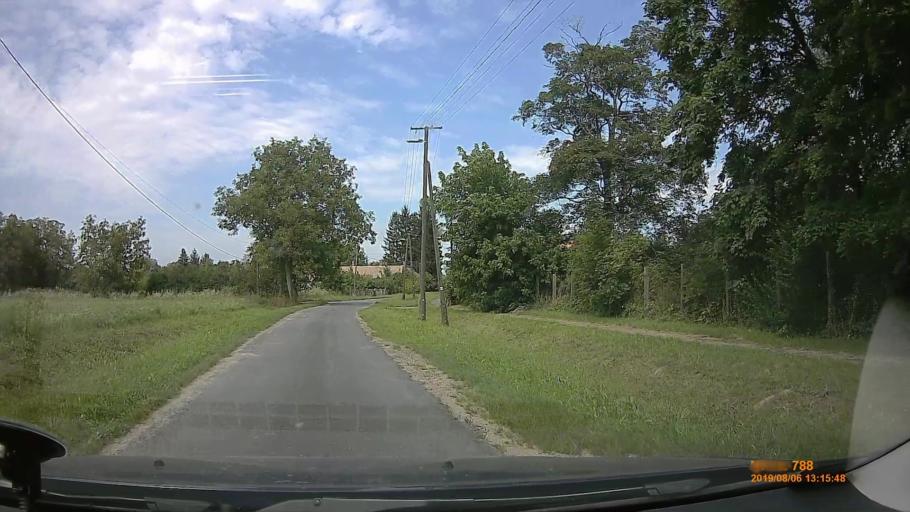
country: HU
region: Zala
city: Pacsa
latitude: 46.6192
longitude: 17.0608
